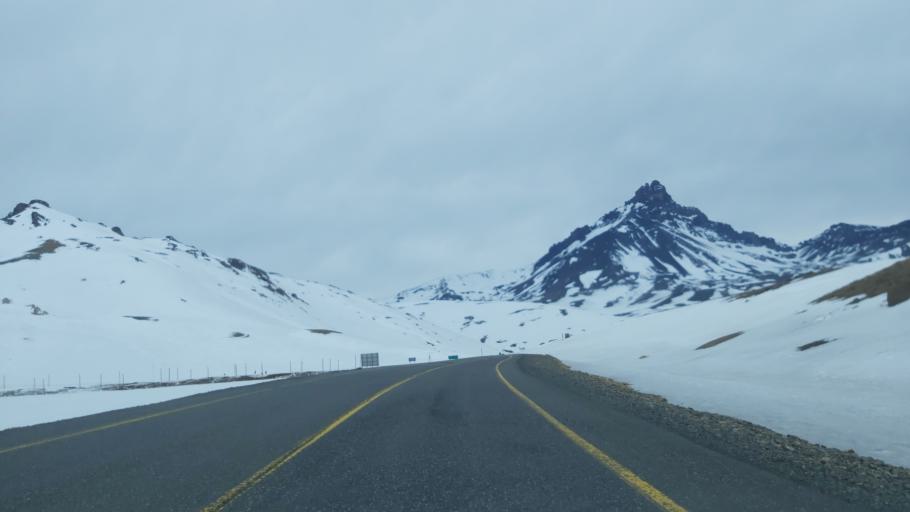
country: AR
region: Mendoza
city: Malargue
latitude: -35.9845
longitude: -70.3943
